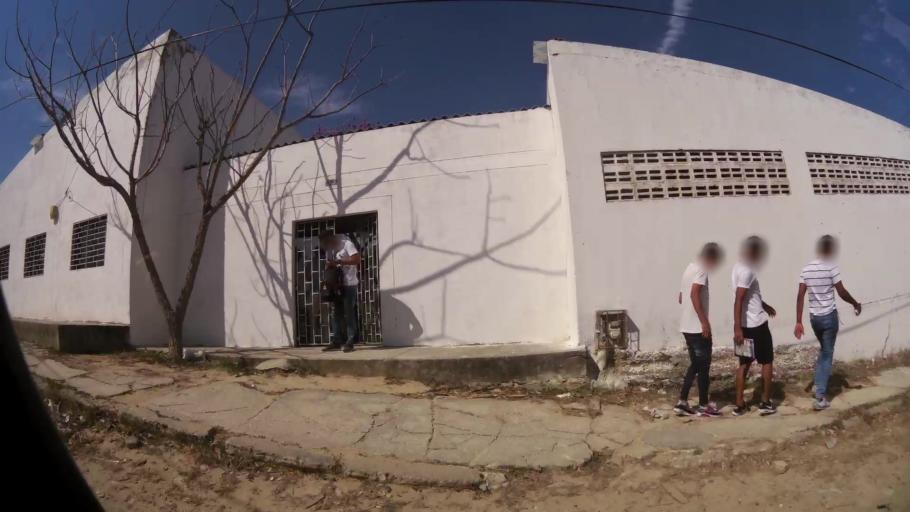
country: CO
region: Atlantico
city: Barranquilla
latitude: 10.9311
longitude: -74.8289
